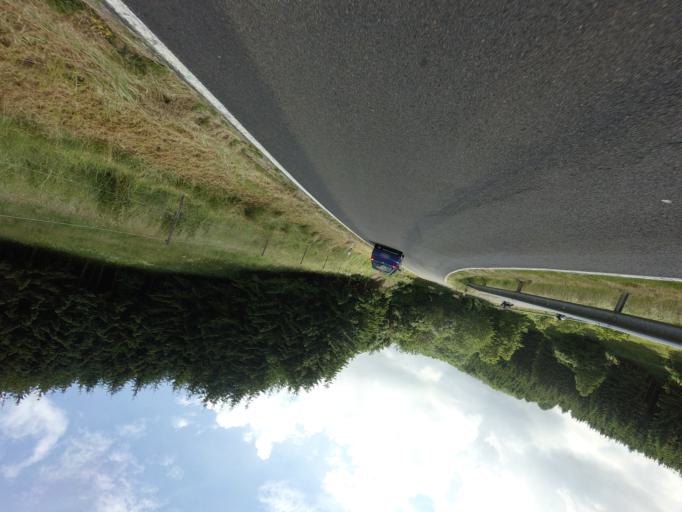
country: DE
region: Rheinland-Pfalz
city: Welschenbach
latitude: 50.3651
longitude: 7.0586
